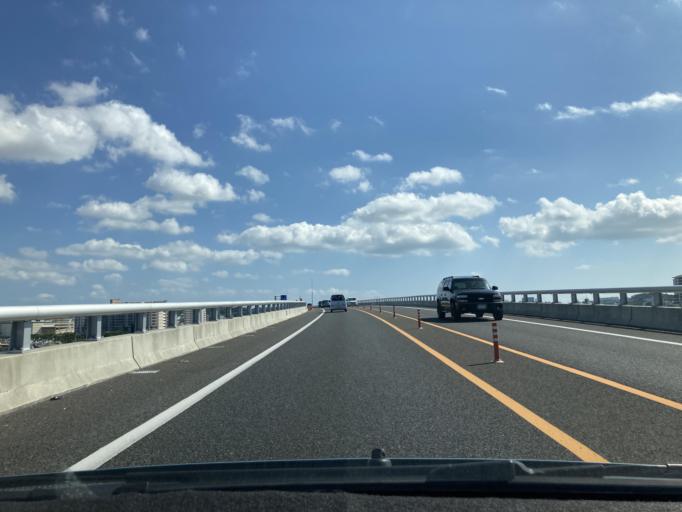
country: JP
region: Okinawa
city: Ginowan
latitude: 26.2730
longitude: 127.7209
